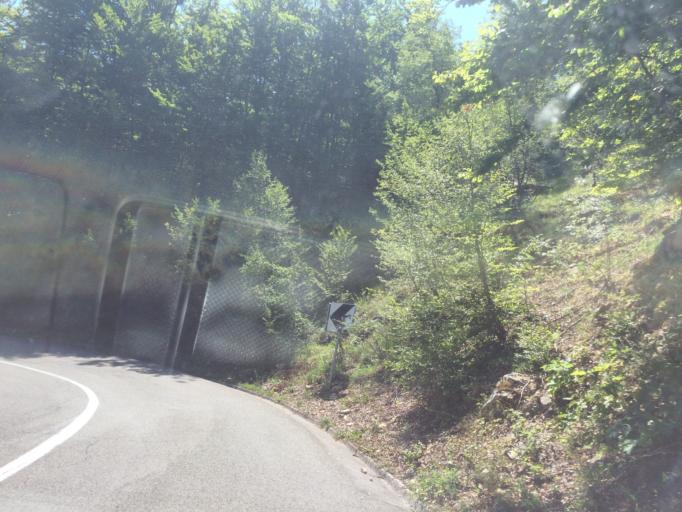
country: ME
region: Opstina Savnik
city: Savnik
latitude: 42.9478
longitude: 19.0952
